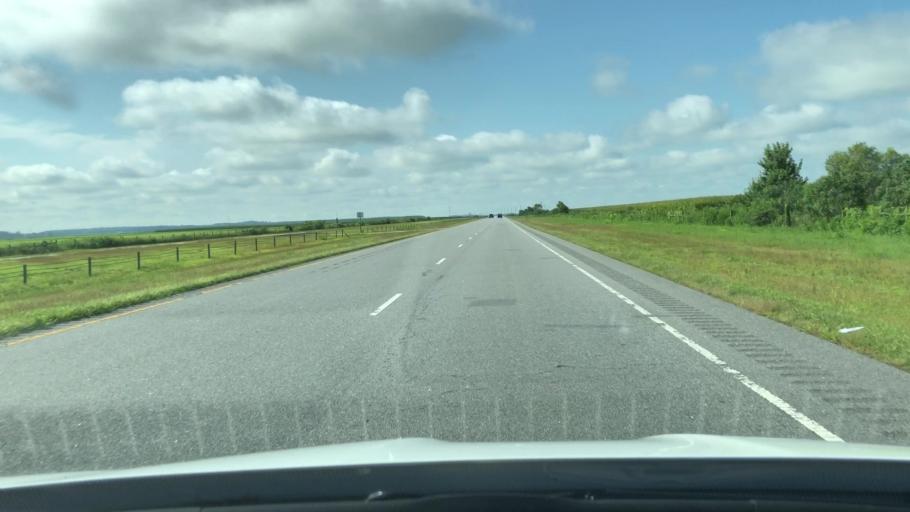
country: US
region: North Carolina
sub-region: Pasquotank County
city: Elizabeth City
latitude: 36.3487
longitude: -76.3141
